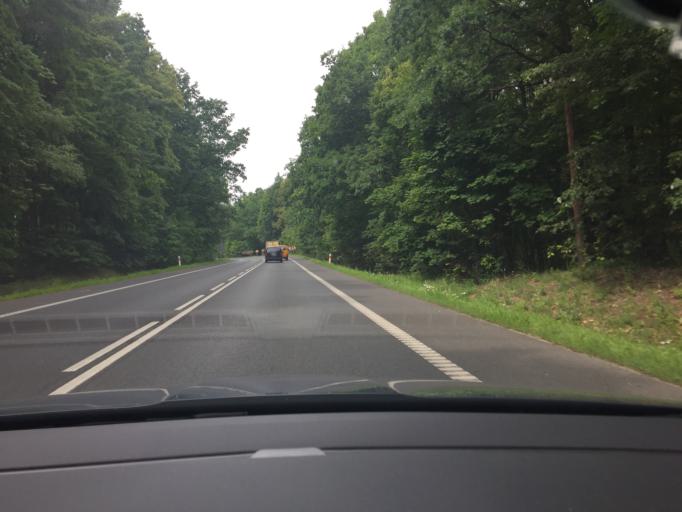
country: PL
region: Kujawsko-Pomorskie
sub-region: Powiat swiecki
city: Nowe
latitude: 53.6355
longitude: 18.6922
